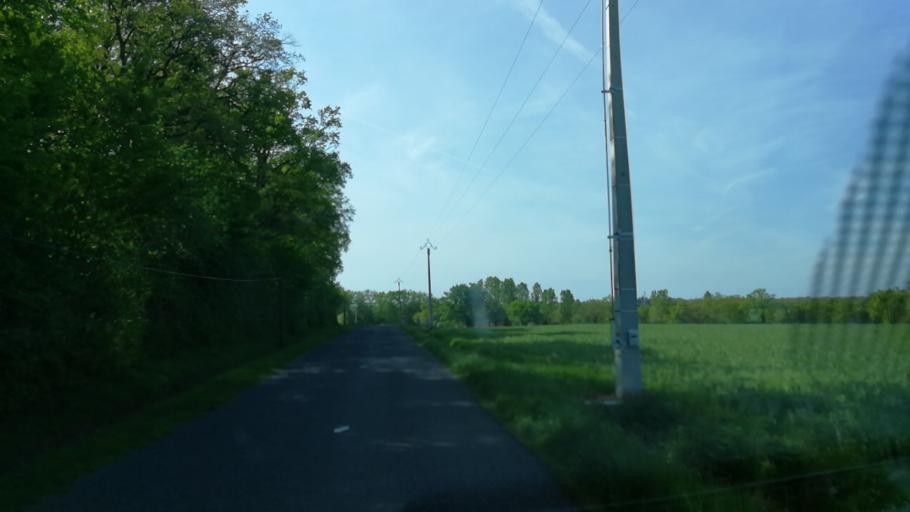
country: FR
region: Auvergne
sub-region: Departement de l'Allier
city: Neuilly-le-Real
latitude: 46.4935
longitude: 3.5148
